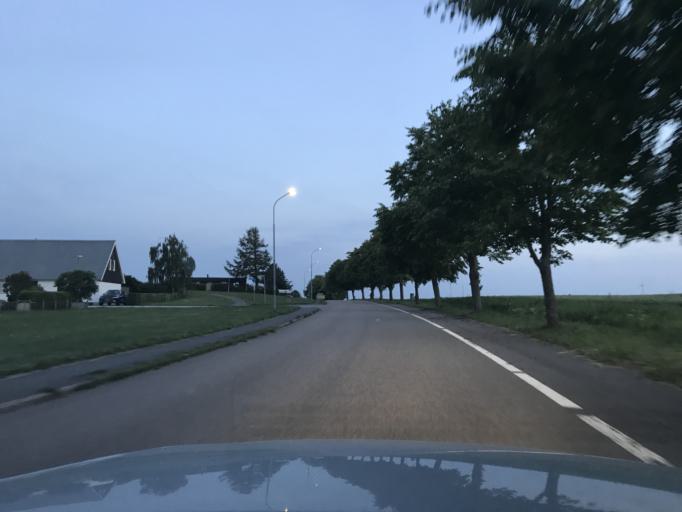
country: SE
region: Skane
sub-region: Svalovs Kommun
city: Svaloev
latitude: 55.9145
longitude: 13.0940
